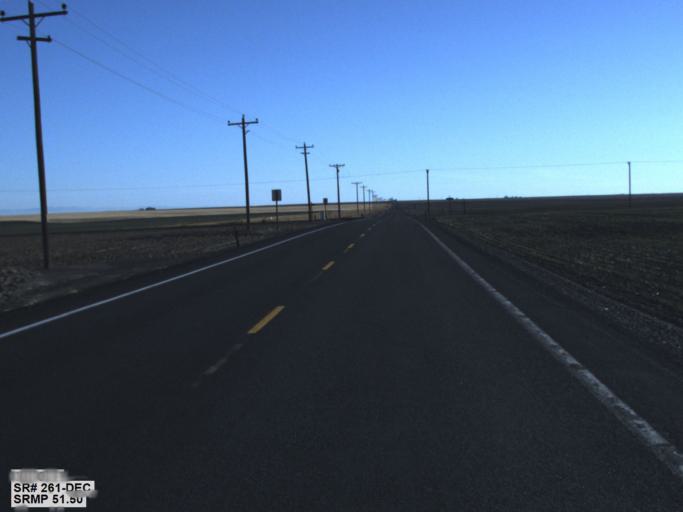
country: US
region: Washington
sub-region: Adams County
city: Ritzville
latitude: 46.9590
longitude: -118.3434
